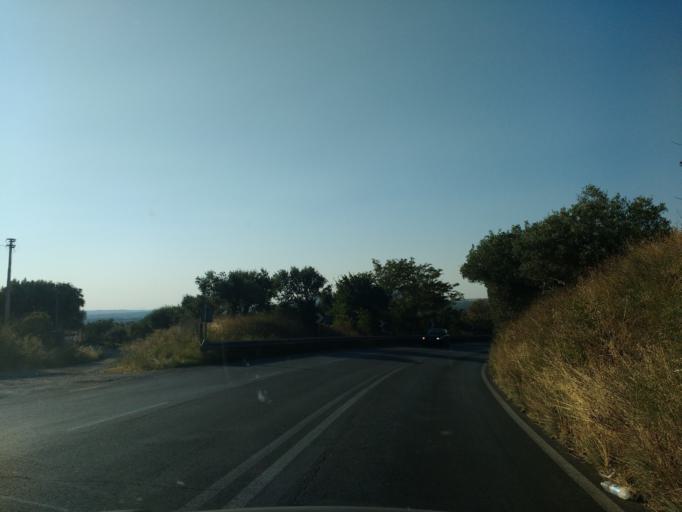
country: IT
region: Latium
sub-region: Citta metropolitana di Roma Capitale
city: Villa Adriana
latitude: 41.9525
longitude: 12.7873
